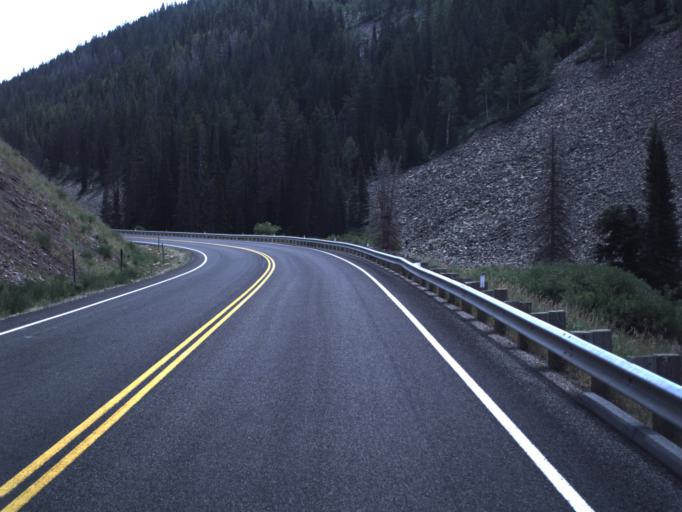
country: US
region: Utah
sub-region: Summit County
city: Francis
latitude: 40.5193
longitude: -111.0826
